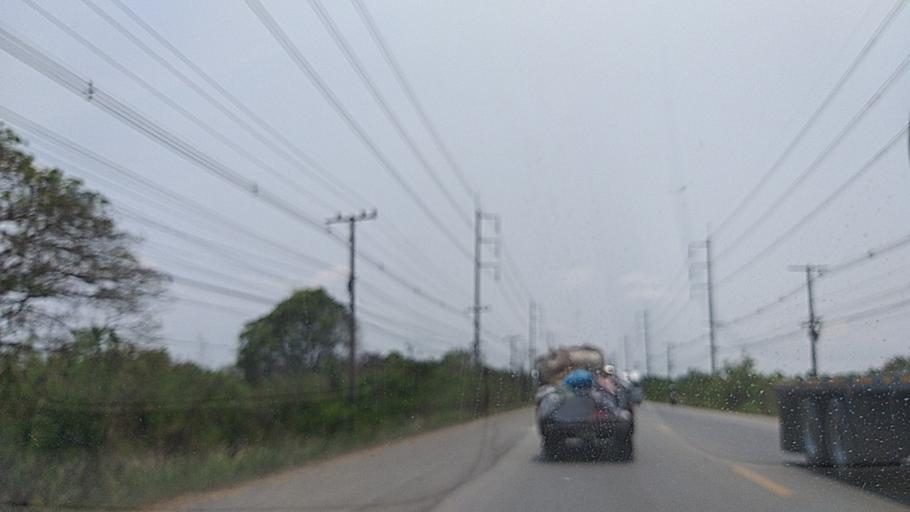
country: TH
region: Chachoengsao
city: Bang Nam Priao
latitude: 13.8073
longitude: 101.0535
